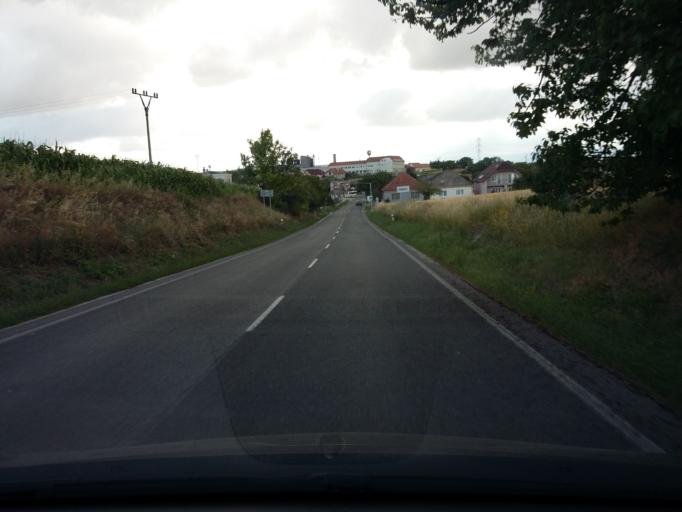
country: SK
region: Trnavsky
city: Vrbove
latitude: 48.5965
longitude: 17.6781
